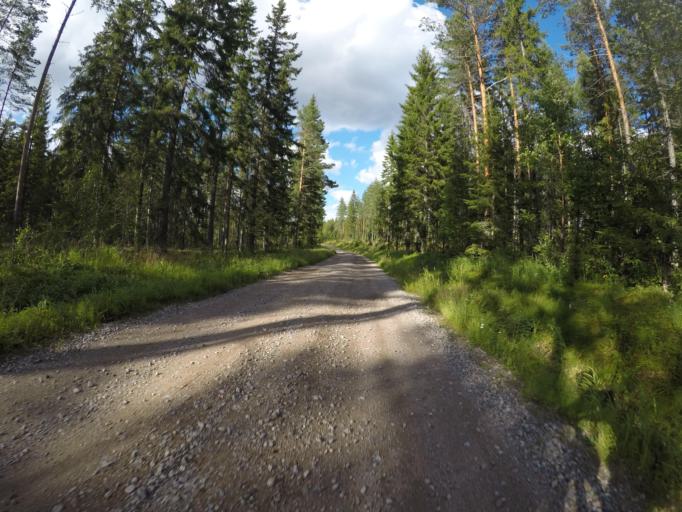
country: SE
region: OErebro
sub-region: Hallefors Kommun
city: Haellefors
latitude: 59.9244
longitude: 14.5661
